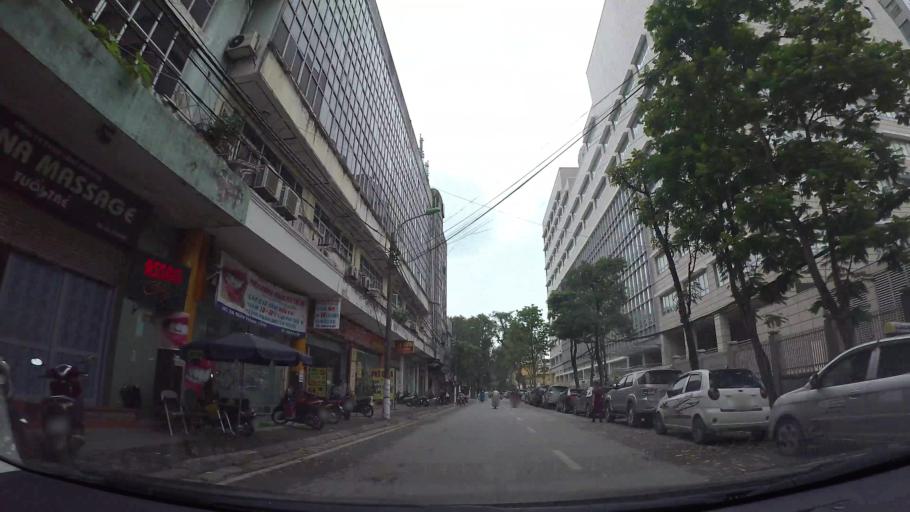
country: VN
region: Ha Noi
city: Hai BaTrung
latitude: 21.0158
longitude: 105.8595
